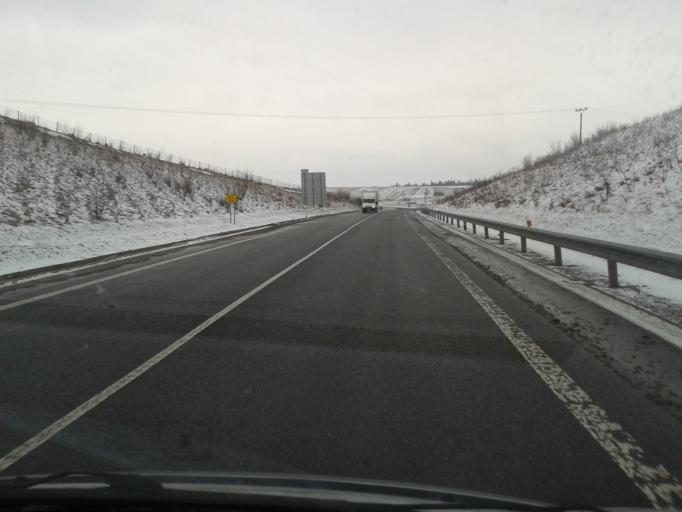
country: SK
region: Zilinsky
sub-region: Okres Zilina
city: Trstena
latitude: 49.3671
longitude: 19.6321
